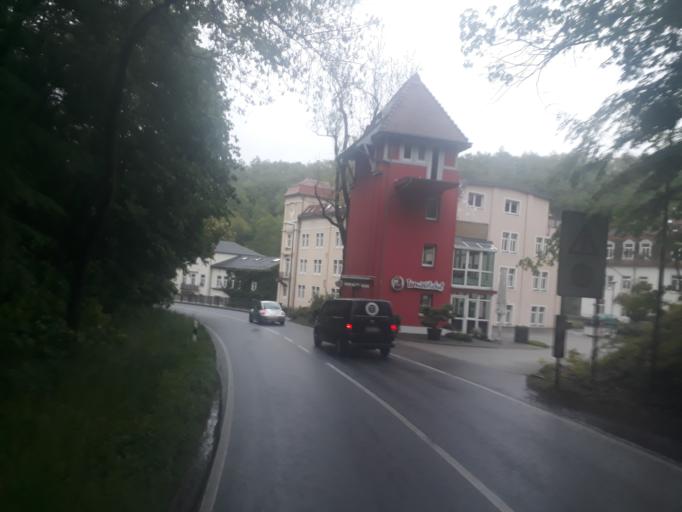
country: DE
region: Saxony
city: Kreischa
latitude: 50.9746
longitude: 13.7847
